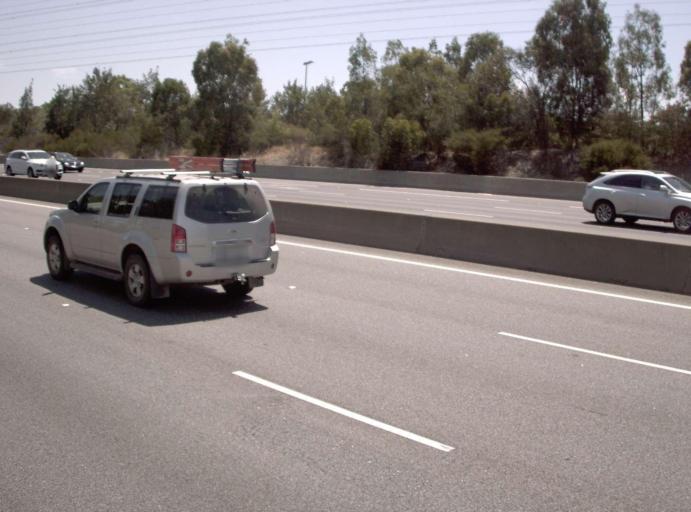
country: AU
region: Victoria
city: Glenferrie
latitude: -37.8402
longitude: 145.0390
